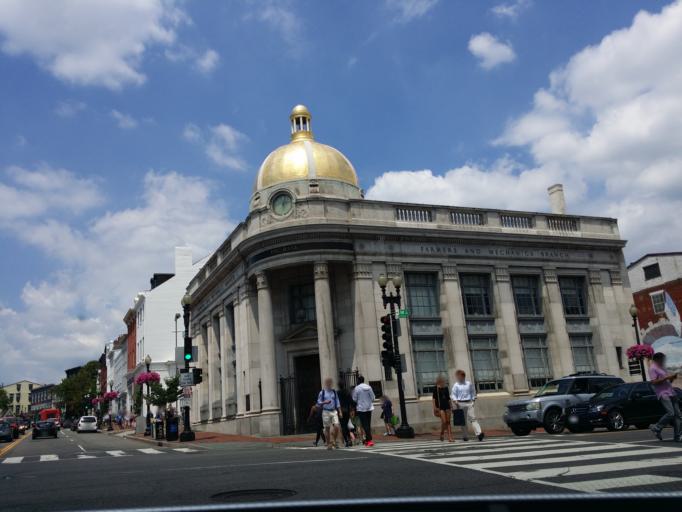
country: US
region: Washington, D.C.
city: Washington, D.C.
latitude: 38.9051
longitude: -77.0628
